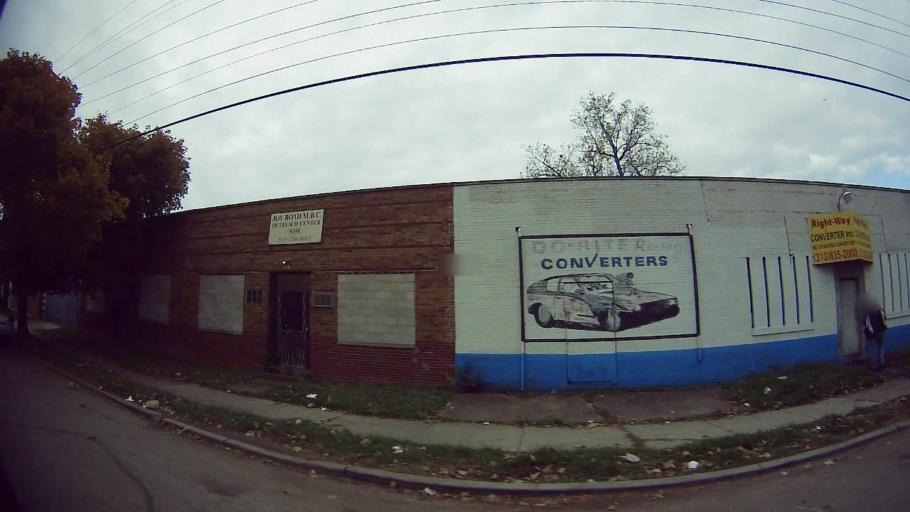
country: US
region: Michigan
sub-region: Wayne County
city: Dearborn
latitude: 42.3646
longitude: -83.1875
